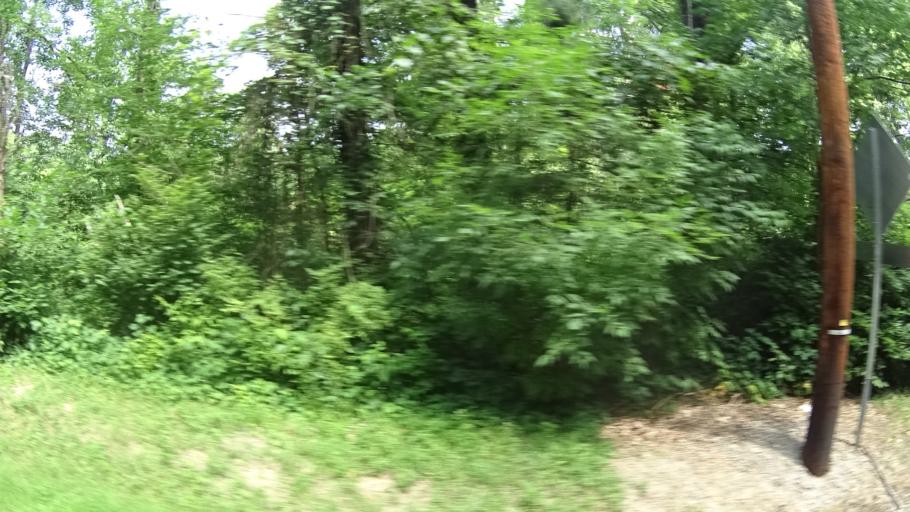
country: US
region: Ohio
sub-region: Lorain County
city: Vermilion
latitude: 41.3865
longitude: -82.3888
